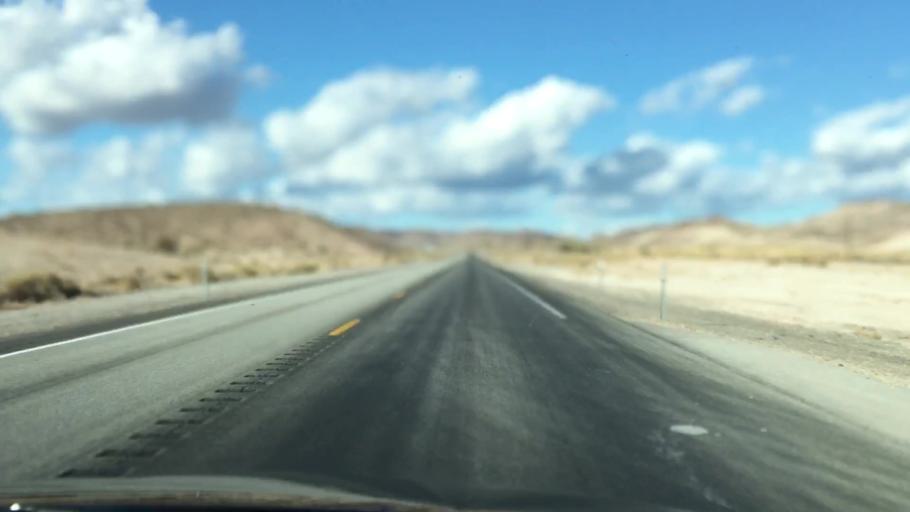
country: US
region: Nevada
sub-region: Nye County
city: Beatty
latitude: 36.9935
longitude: -116.7253
